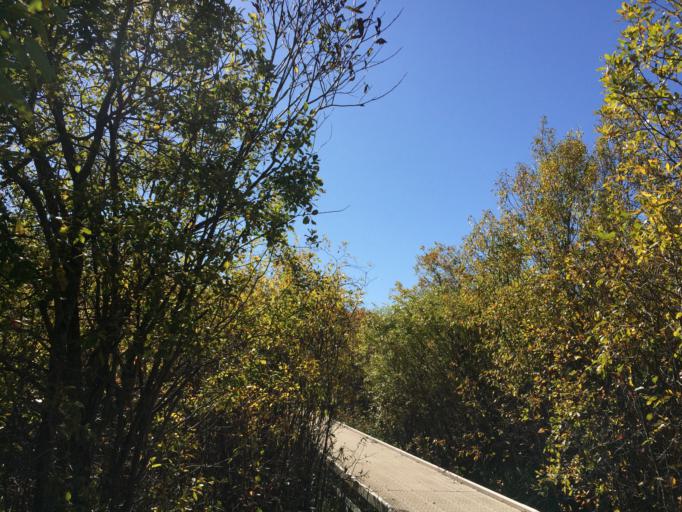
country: US
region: Minnesota
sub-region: Lake of the Woods County
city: Baudette
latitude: 48.2879
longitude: -94.5675
